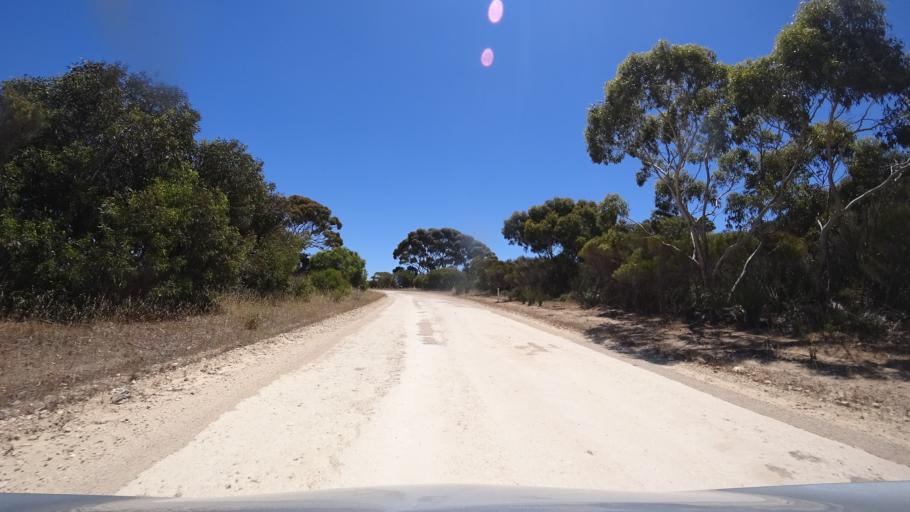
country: AU
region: South Australia
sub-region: Kangaroo Island
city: Kingscote
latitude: -35.6665
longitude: 137.1023
